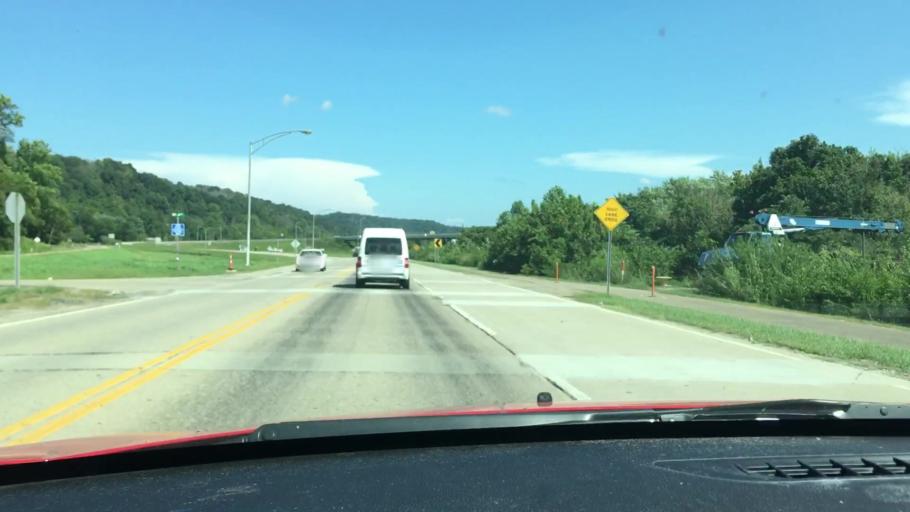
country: US
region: Ohio
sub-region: Athens County
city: Athens
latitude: 39.3345
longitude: -82.0407
